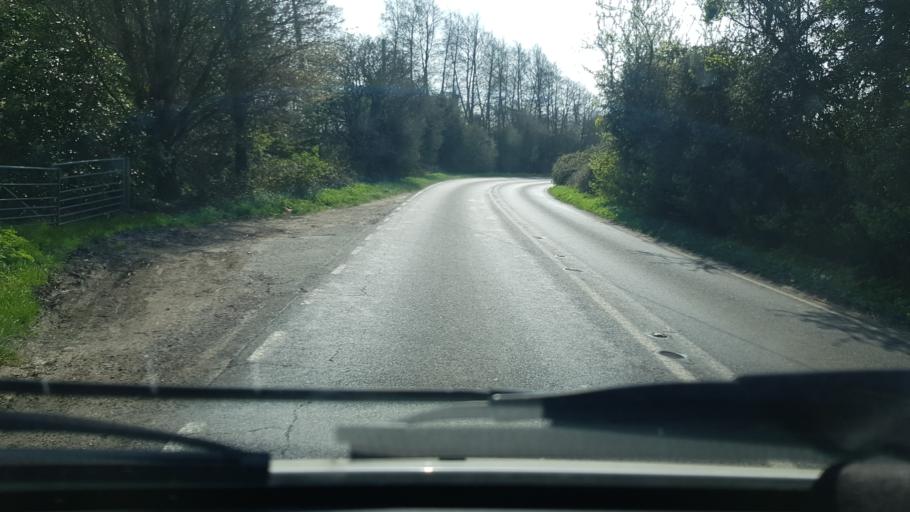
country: GB
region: England
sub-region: West Sussex
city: Birdham
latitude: 50.8097
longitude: -0.8028
